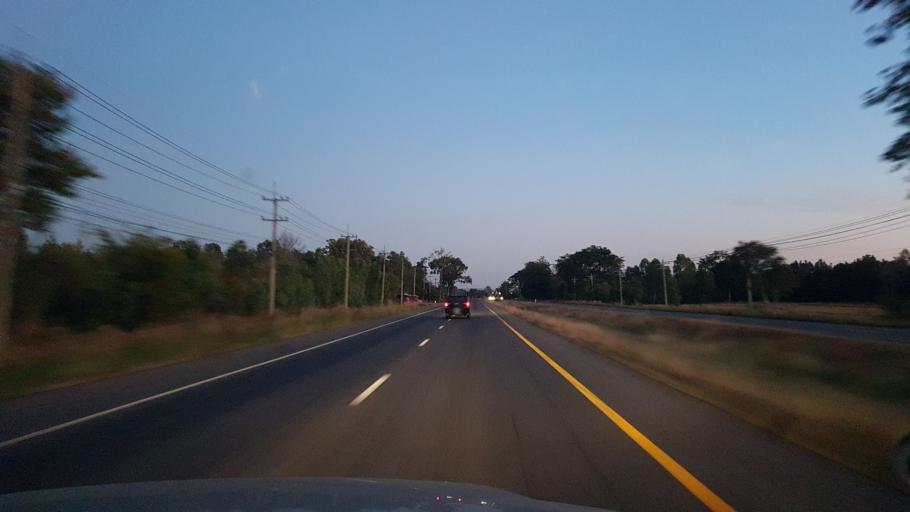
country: TH
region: Chaiyaphum
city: Phu Khiao
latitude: 16.3100
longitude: 102.2024
